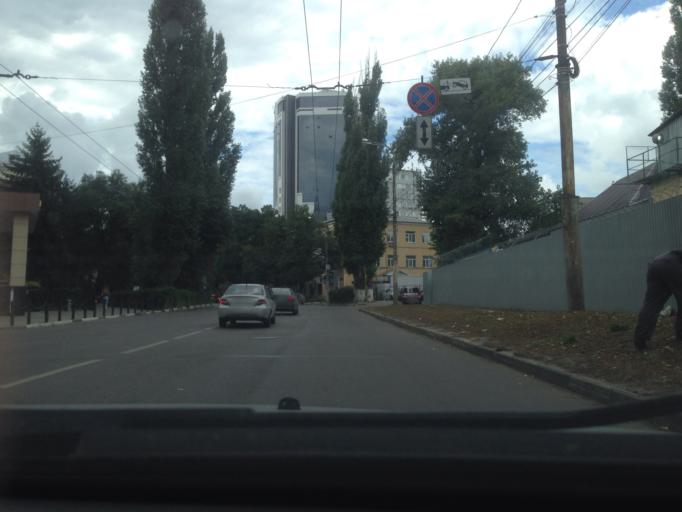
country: RU
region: Voronezj
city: Voronezh
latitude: 51.6745
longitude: 39.1881
